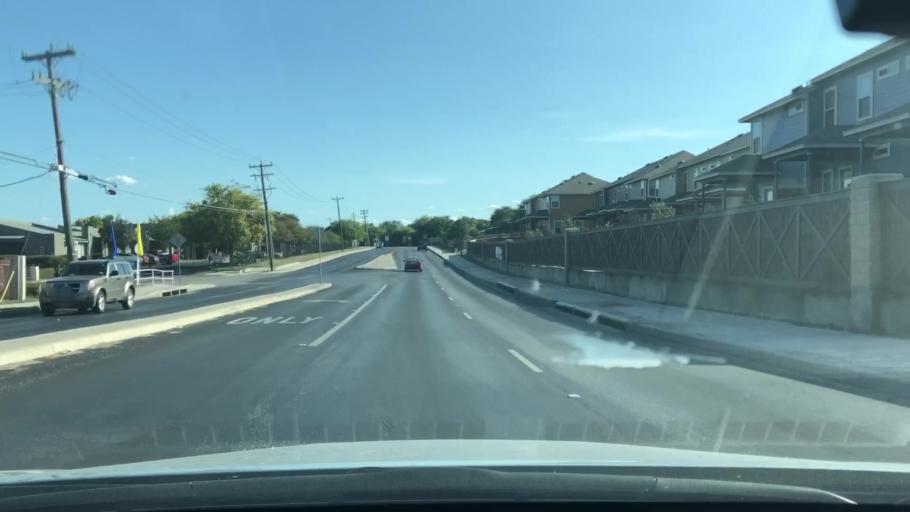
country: US
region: Texas
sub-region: Bexar County
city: Kirby
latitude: 29.4819
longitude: -98.3476
